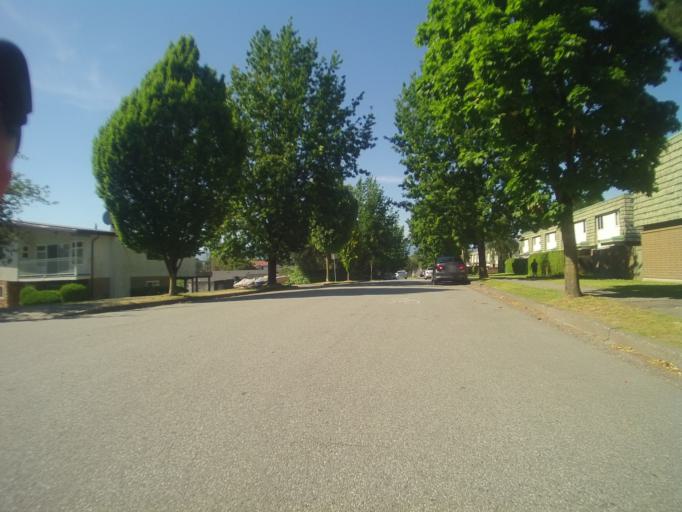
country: CA
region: British Columbia
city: Vancouver
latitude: 49.2277
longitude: -123.0799
